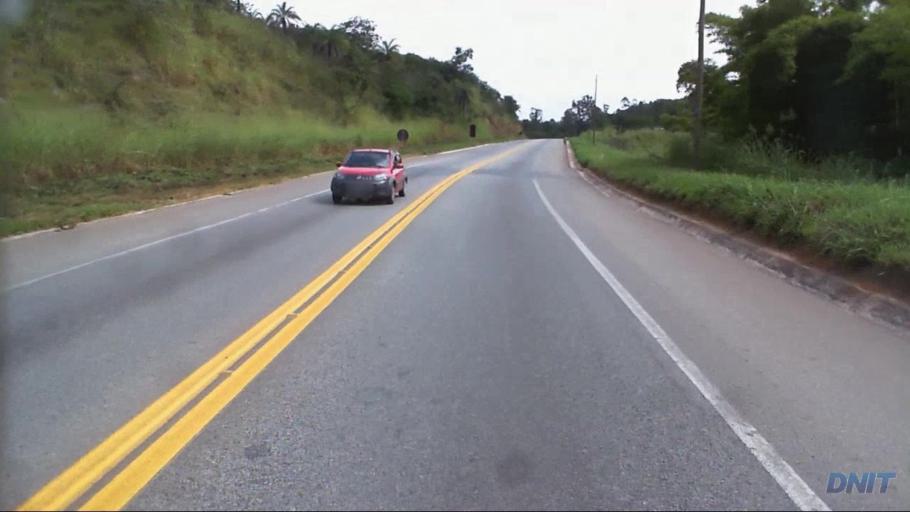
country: BR
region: Minas Gerais
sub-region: Santa Luzia
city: Santa Luzia
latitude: -19.8284
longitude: -43.8400
